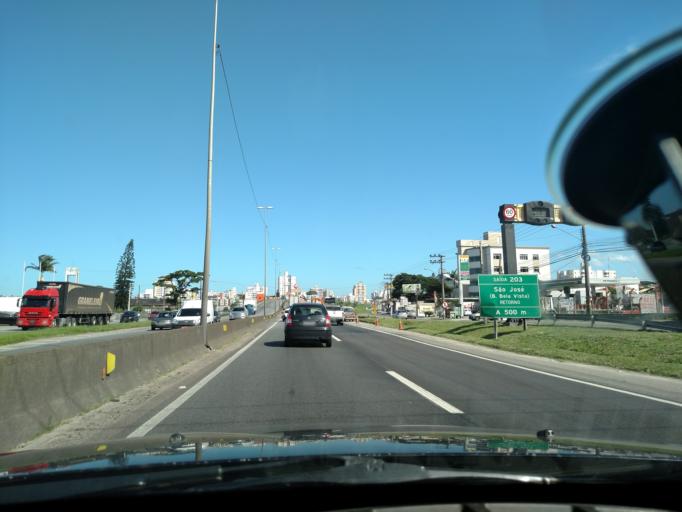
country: BR
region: Santa Catarina
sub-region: Sao Jose
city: Campinas
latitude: -27.5628
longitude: -48.6158
